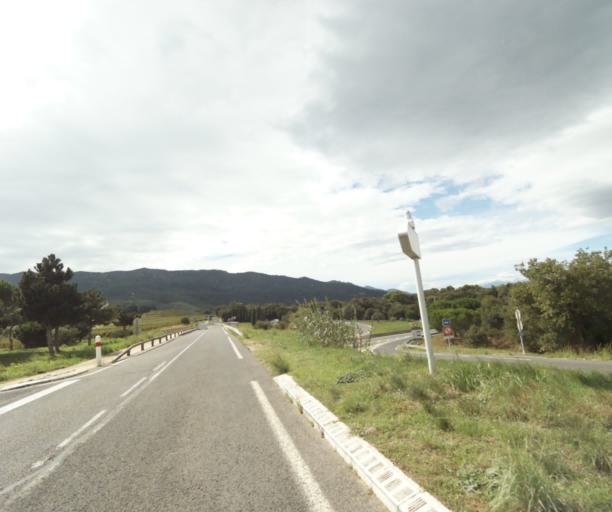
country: FR
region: Languedoc-Roussillon
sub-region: Departement des Pyrenees-Orientales
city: Argelers
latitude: 42.5368
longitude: 3.0332
